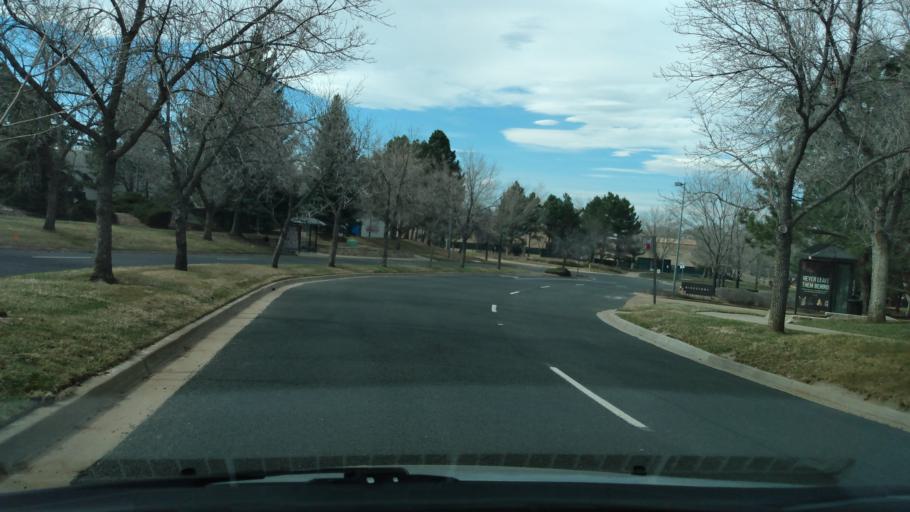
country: US
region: Colorado
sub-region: Broomfield County
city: Broomfield
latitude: 39.9185
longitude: -105.1122
